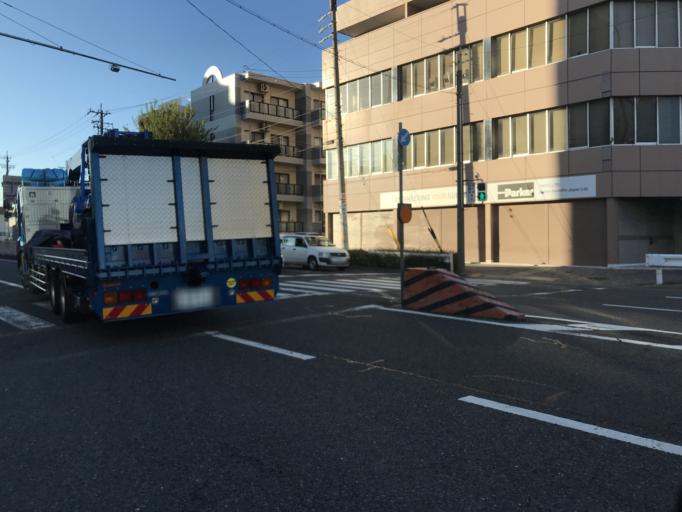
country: JP
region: Aichi
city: Nagoya-shi
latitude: 35.1776
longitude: 136.8728
